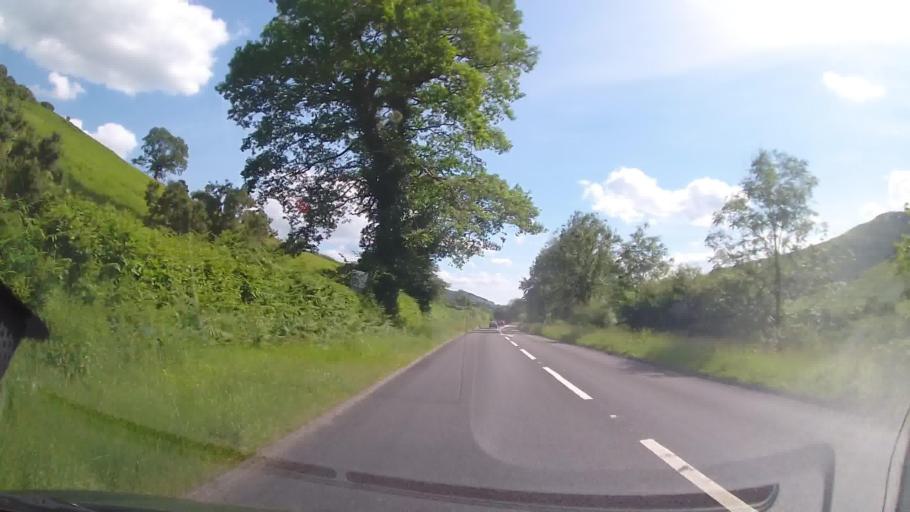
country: GB
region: Wales
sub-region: Gwynedd
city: Corris
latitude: 52.7054
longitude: -3.6864
